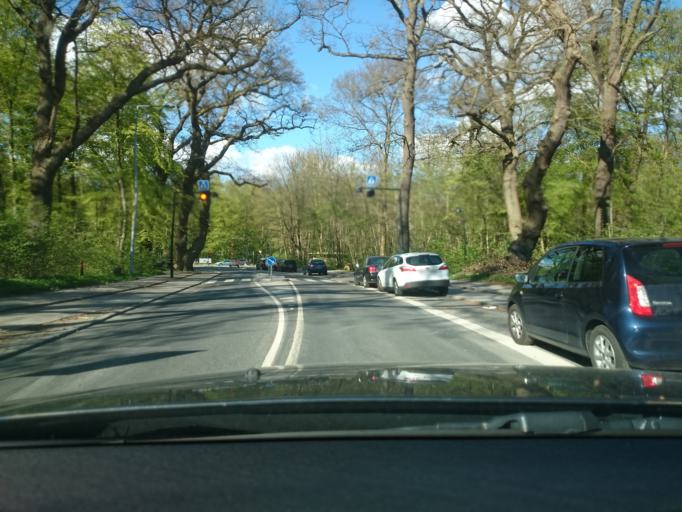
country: DK
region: Capital Region
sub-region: Gentofte Kommune
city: Charlottenlund
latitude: 55.7681
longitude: 12.5600
